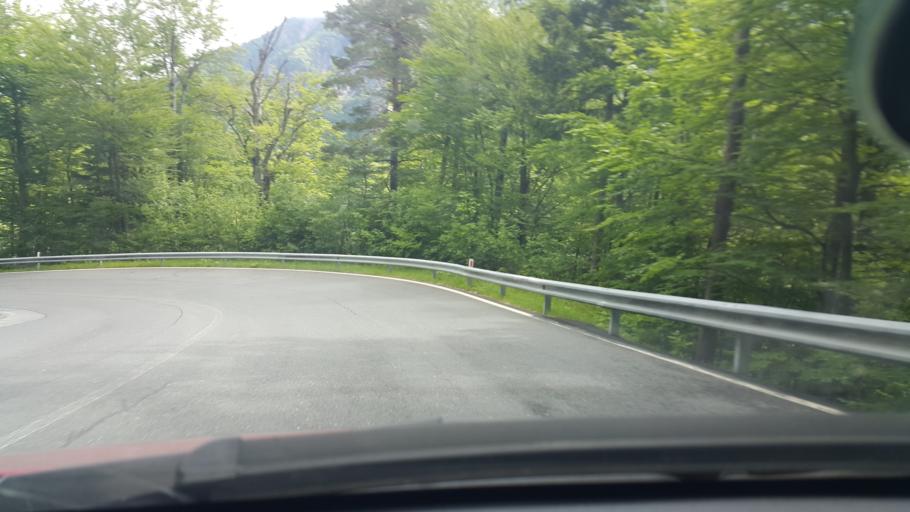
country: AT
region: Carinthia
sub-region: Politischer Bezirk Klagenfurt Land
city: Ferlach
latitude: 46.4934
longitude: 14.2803
